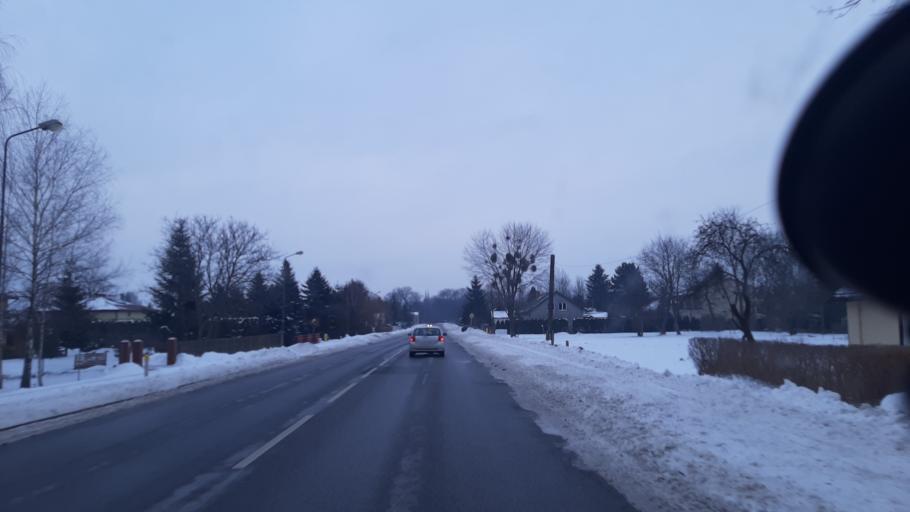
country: PL
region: Lublin Voivodeship
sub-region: Powiat lubelski
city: Garbow
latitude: 51.3571
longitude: 22.3225
